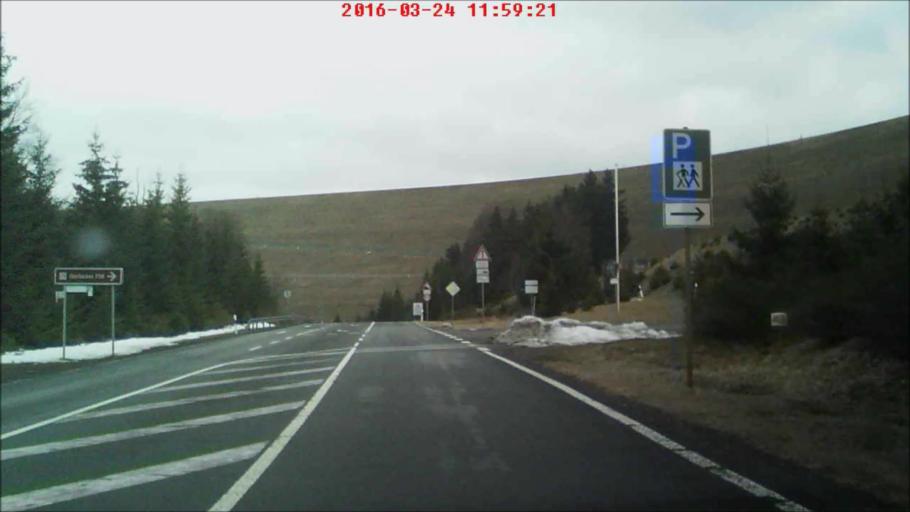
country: DE
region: Thuringia
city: Goldisthal
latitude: 50.5020
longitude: 11.0300
